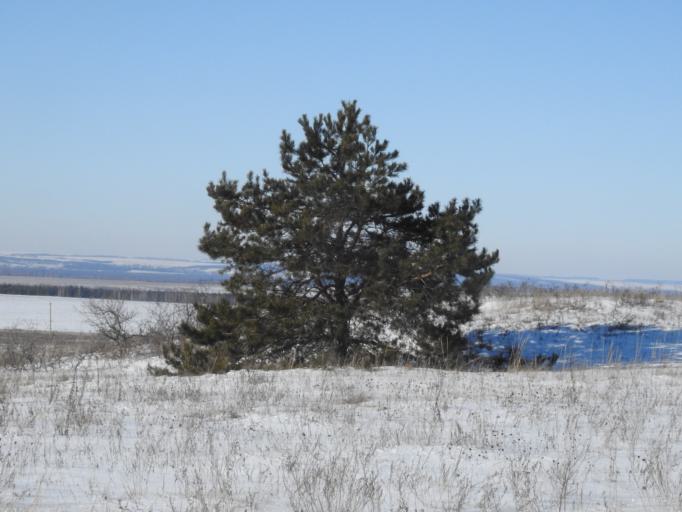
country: RU
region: Saratov
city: Lysyye Gory
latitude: 51.4698
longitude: 44.9654
